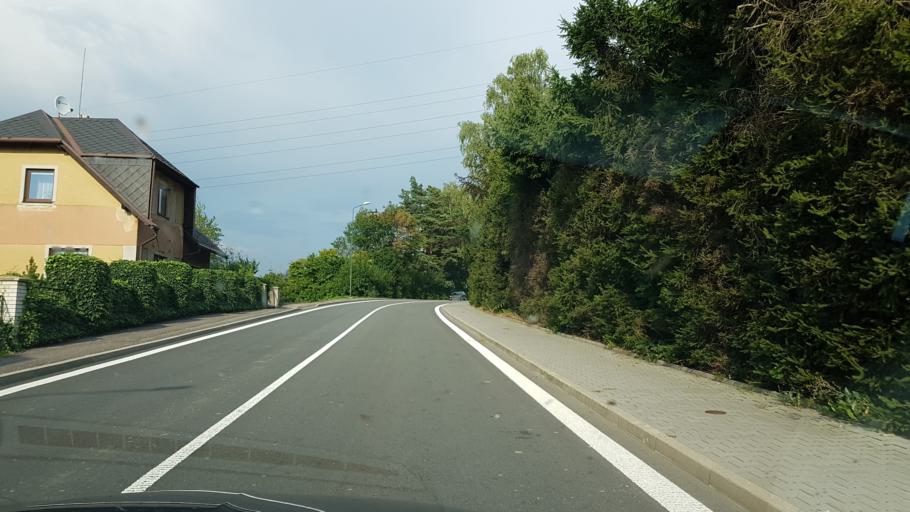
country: CZ
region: Pardubicky
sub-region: Okres Usti nad Orlici
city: Kraliky
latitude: 50.0828
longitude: 16.7507
